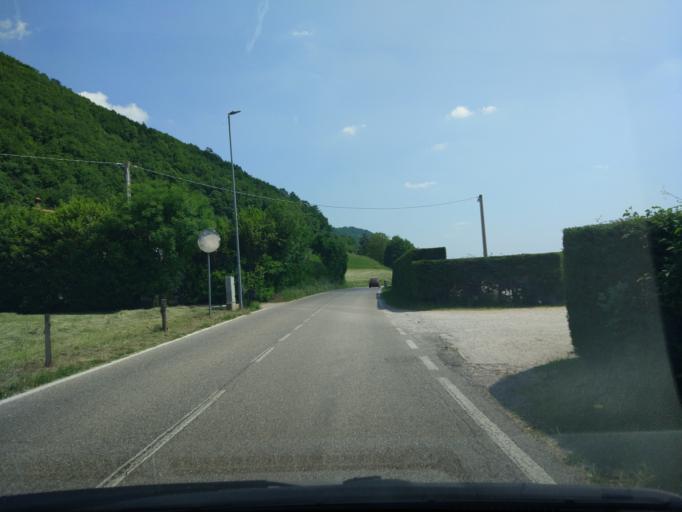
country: IT
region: Veneto
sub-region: Provincia di Verona
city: Badia Calavena
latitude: 45.5748
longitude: 11.1517
